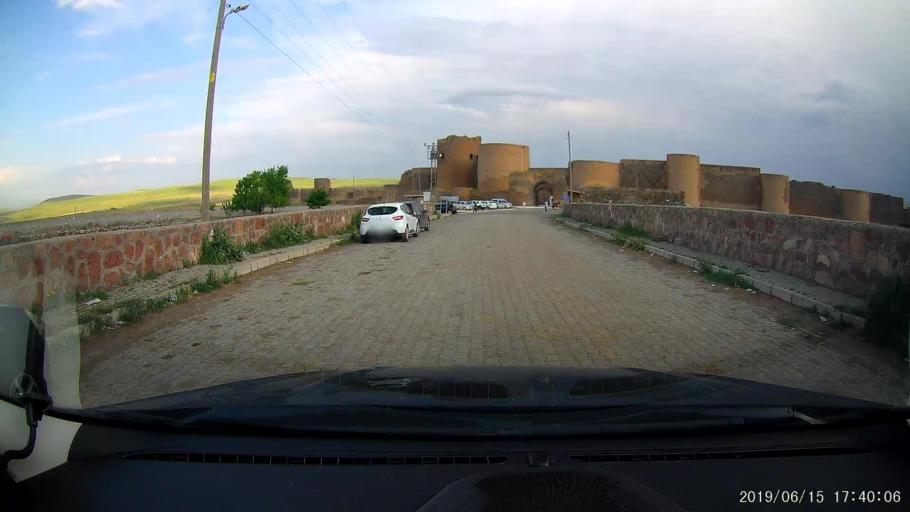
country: TR
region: Kars
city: Basgedikler
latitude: 40.5130
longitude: 43.5721
